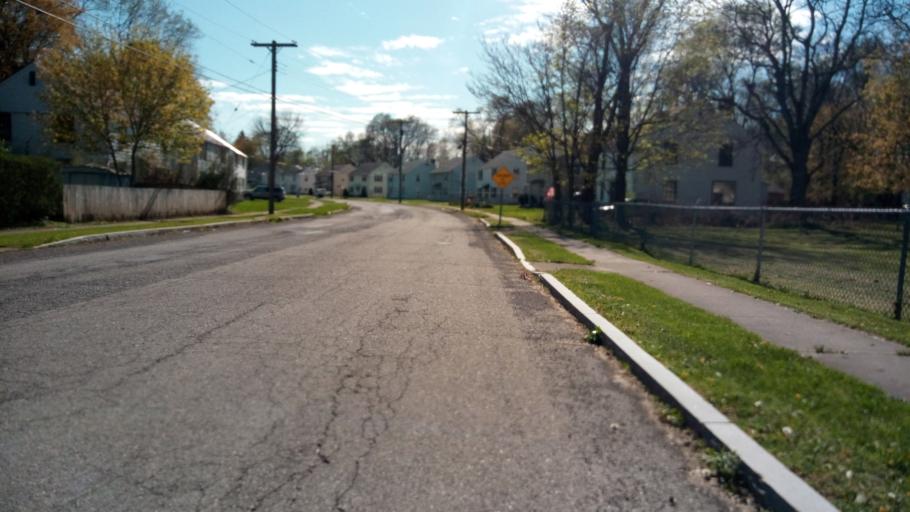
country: US
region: New York
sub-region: Chemung County
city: Elmira
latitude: 42.0681
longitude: -76.7997
